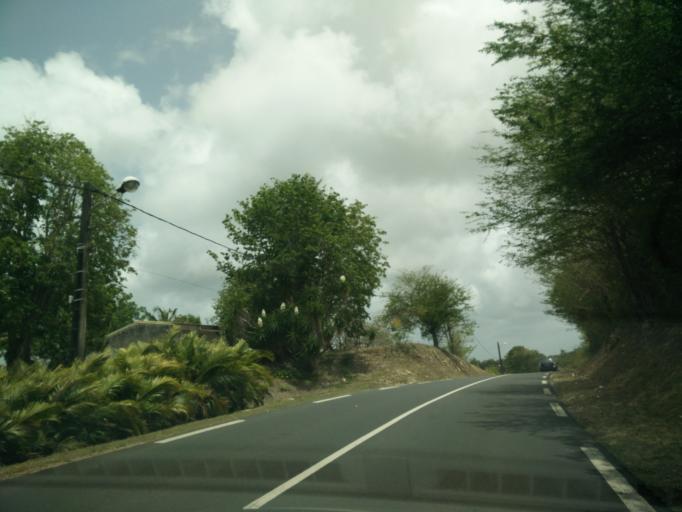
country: GP
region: Guadeloupe
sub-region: Guadeloupe
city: Petit-Canal
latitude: 16.3697
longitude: -61.4632
